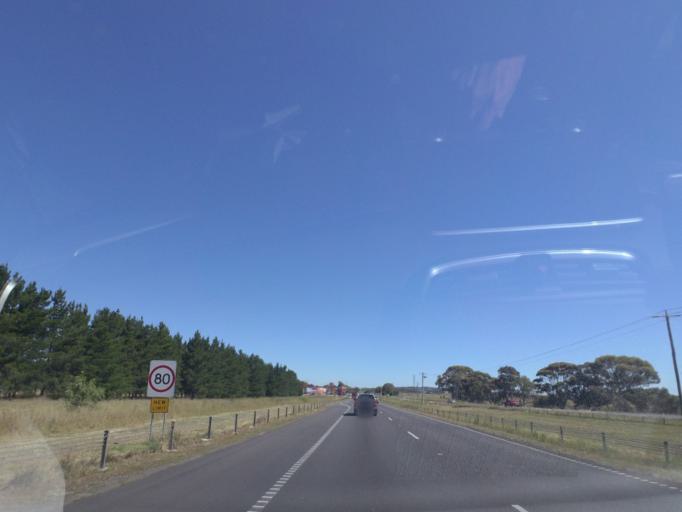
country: AU
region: Victoria
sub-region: Hume
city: Craigieburn
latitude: -37.5228
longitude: 144.9485
